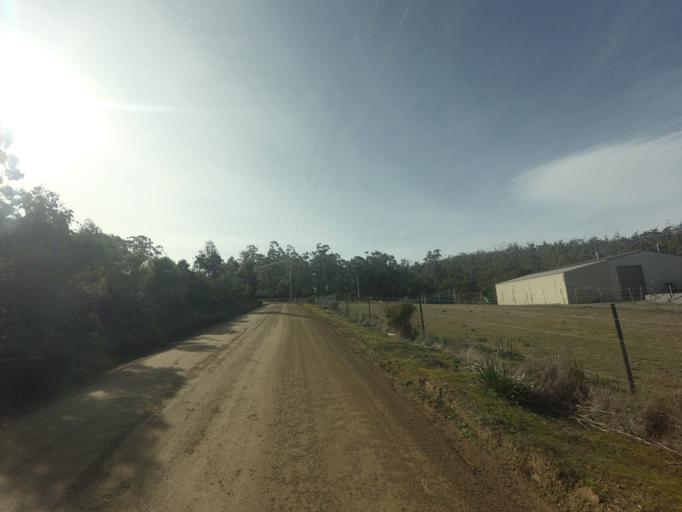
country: AU
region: Tasmania
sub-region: Kingborough
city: Kettering
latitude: -43.0930
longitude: 147.2645
